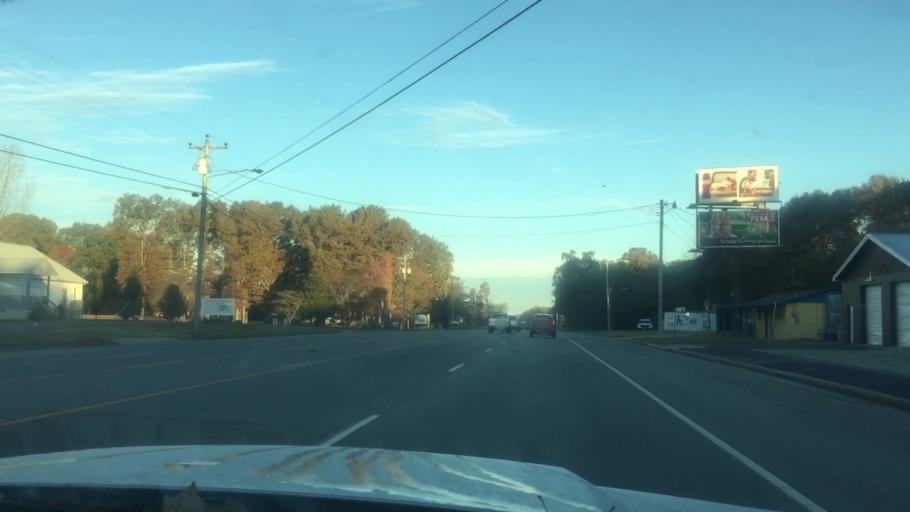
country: US
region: Tennessee
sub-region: Franklin County
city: Estill Springs
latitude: 35.2874
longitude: -86.1429
